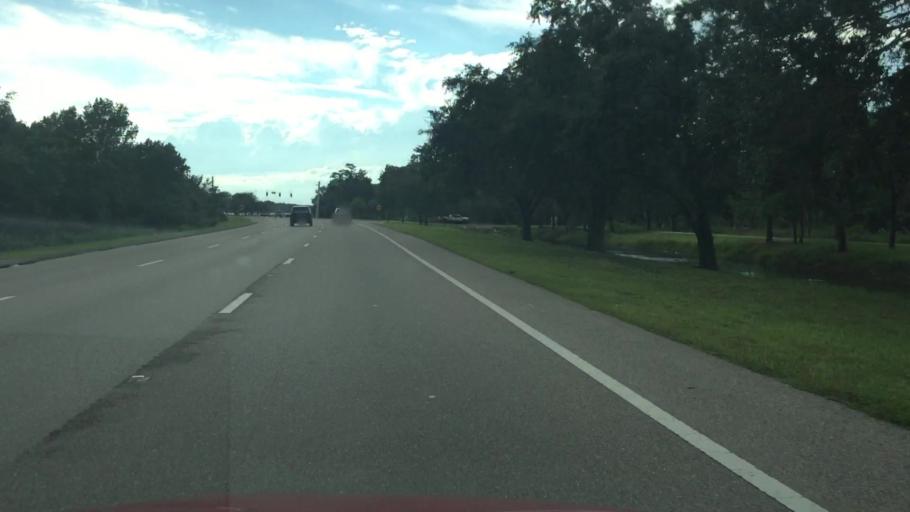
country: US
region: Florida
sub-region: Lee County
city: Villas
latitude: 26.5475
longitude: -81.8138
